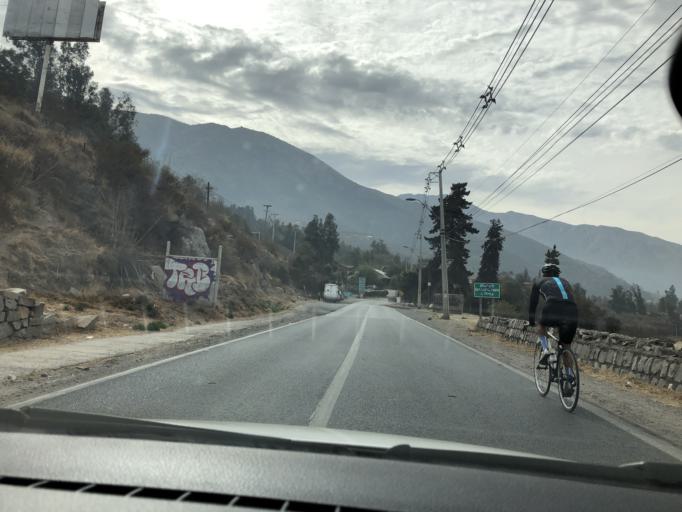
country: CL
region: Santiago Metropolitan
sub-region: Provincia de Cordillera
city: Puente Alto
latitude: -33.5955
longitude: -70.4909
